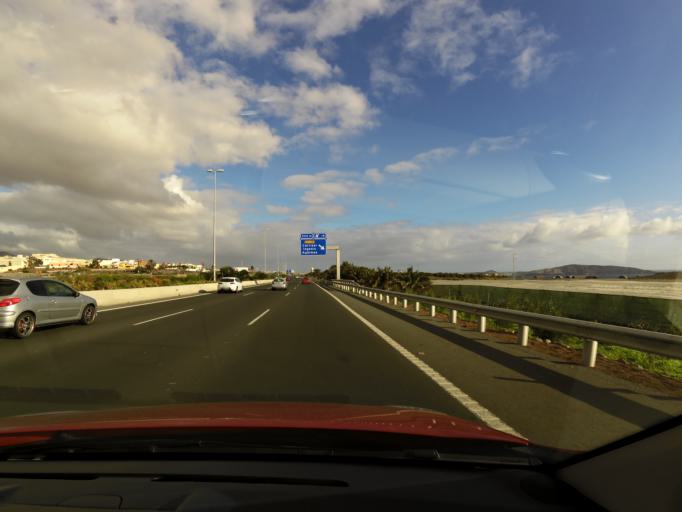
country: ES
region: Canary Islands
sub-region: Provincia de Las Palmas
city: Ingenio
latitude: 27.9113
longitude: -15.3991
